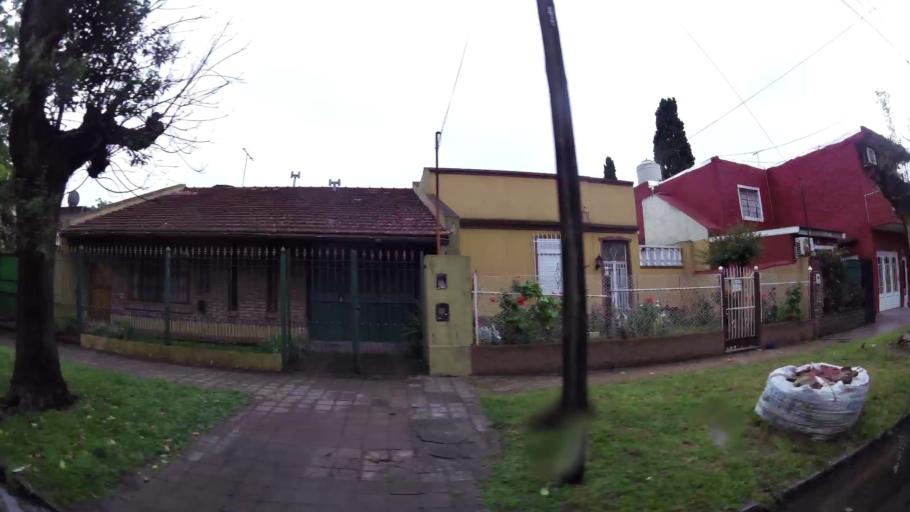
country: AR
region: Buenos Aires
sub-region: Partido de Lomas de Zamora
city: Lomas de Zamora
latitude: -34.7382
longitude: -58.3873
